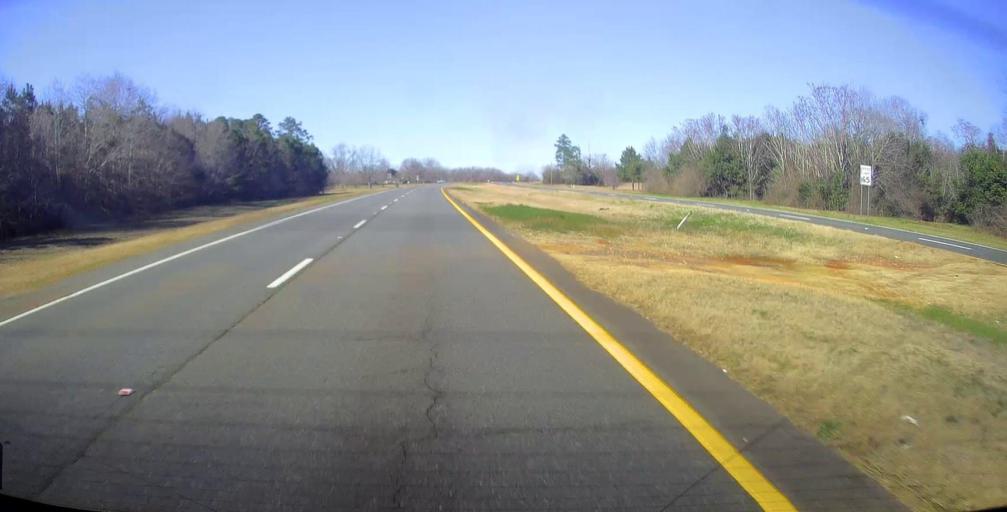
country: US
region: Georgia
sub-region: Sumter County
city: Americus
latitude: 32.1530
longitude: -84.2702
